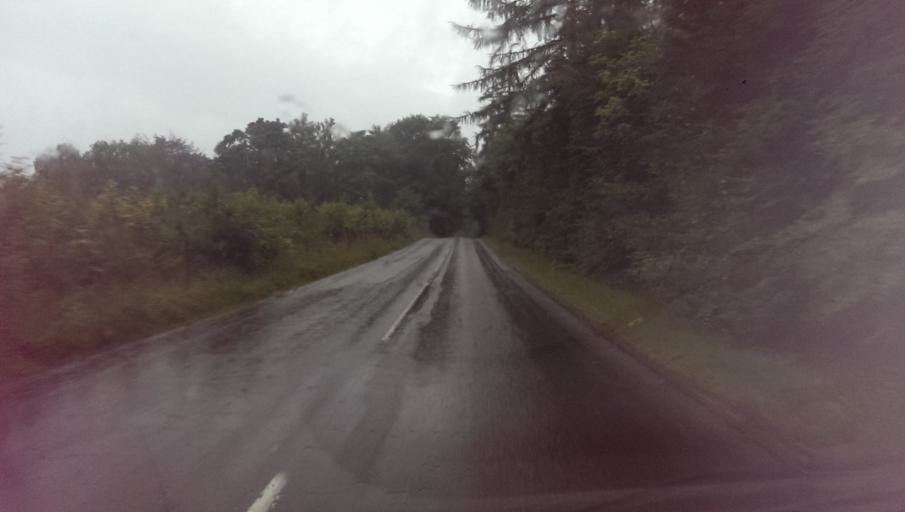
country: DK
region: Central Jutland
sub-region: Silkeborg Kommune
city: Virklund
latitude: 56.0763
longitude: 9.4095
